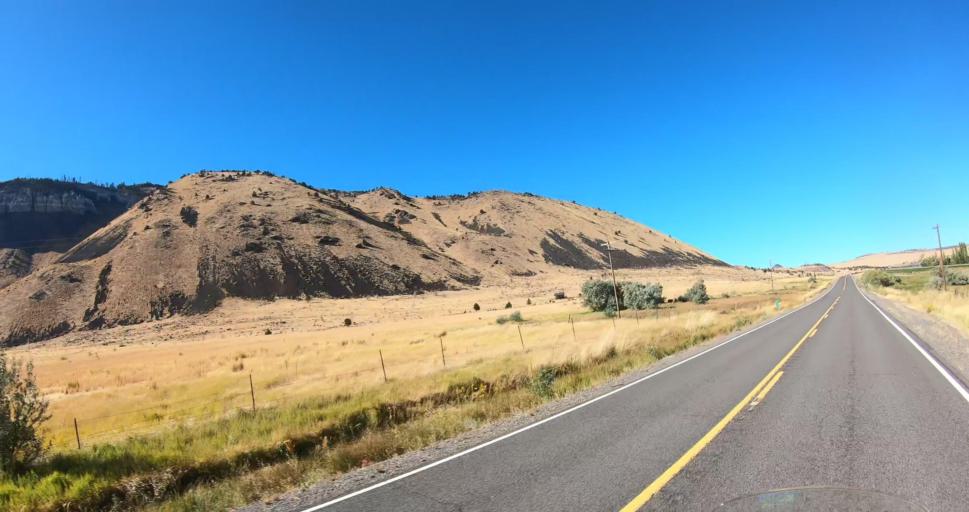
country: US
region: Oregon
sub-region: Lake County
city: Lakeview
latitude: 42.9861
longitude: -120.7772
